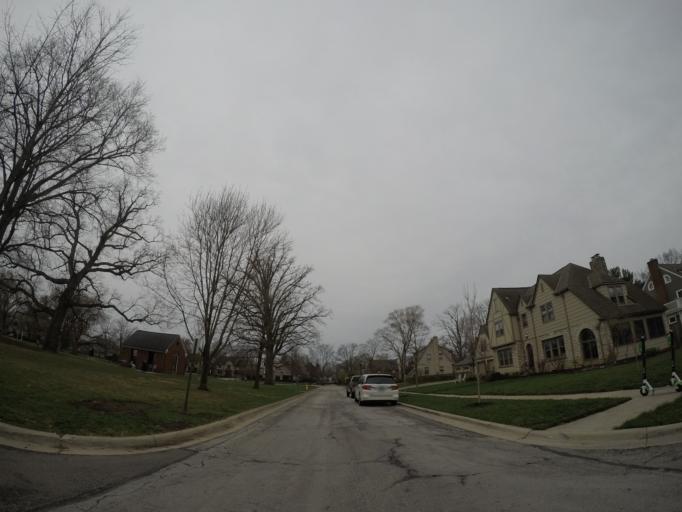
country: US
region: Ohio
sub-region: Franklin County
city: Upper Arlington
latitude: 40.0034
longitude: -83.0657
